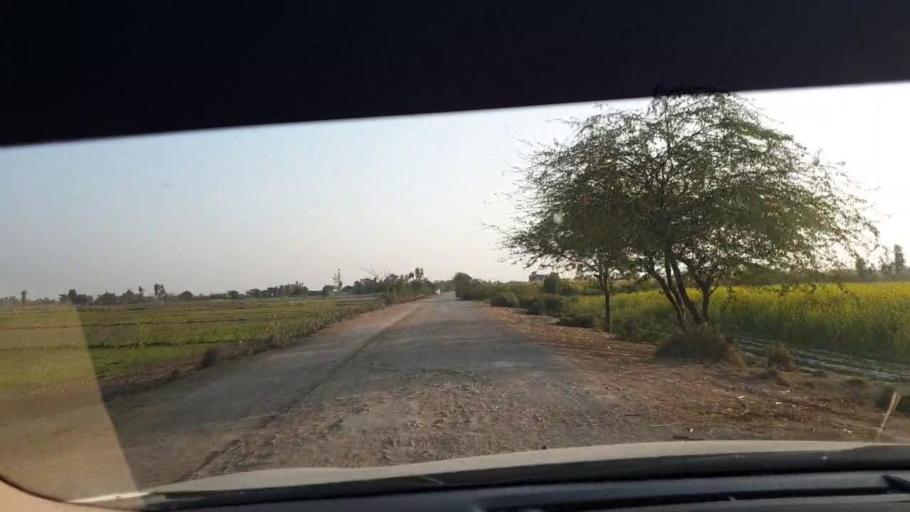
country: PK
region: Sindh
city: Berani
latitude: 25.8425
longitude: 68.8168
